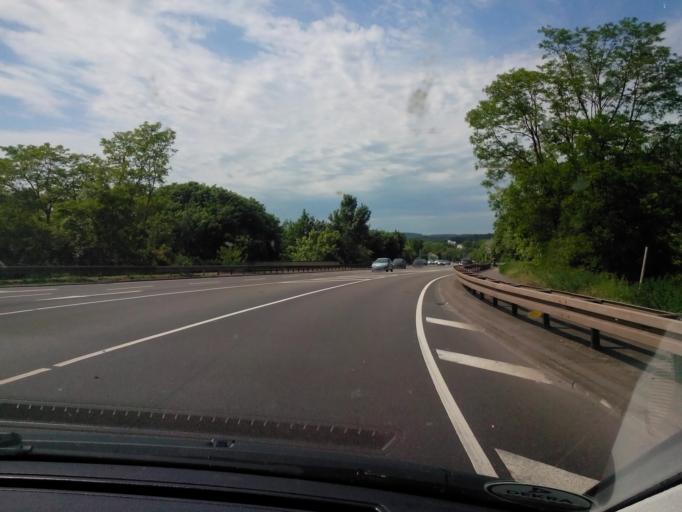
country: DE
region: Saarland
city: Dillingen
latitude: 49.3453
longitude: 6.7366
